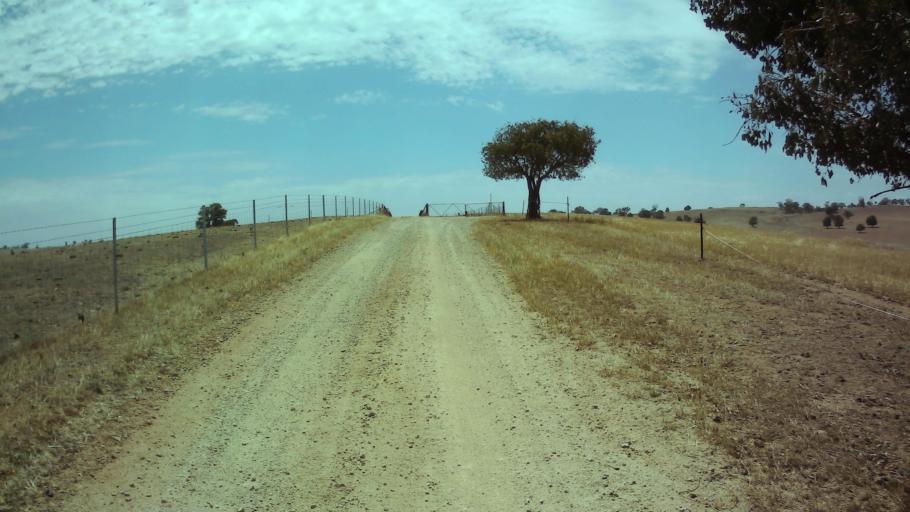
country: AU
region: New South Wales
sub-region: Cowra
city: Cowra
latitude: -33.9580
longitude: 148.4553
